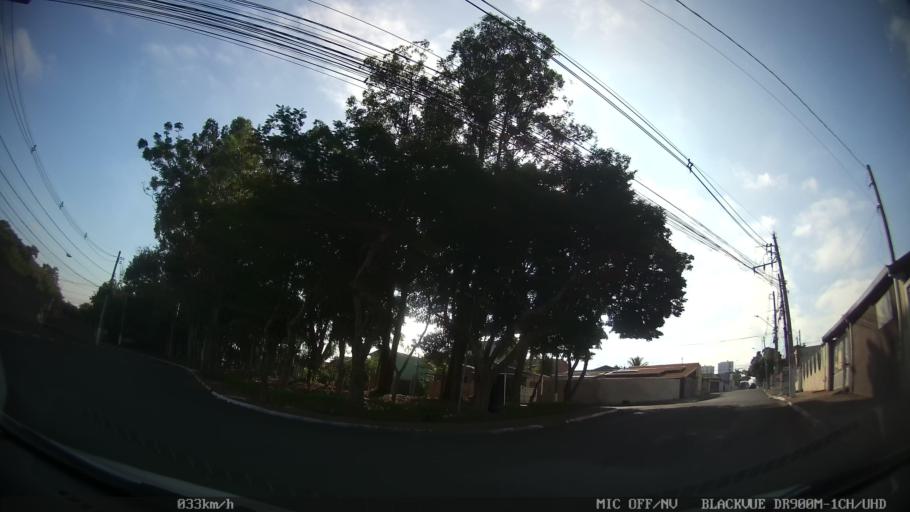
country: BR
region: Sao Paulo
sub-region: Hortolandia
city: Hortolandia
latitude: -22.9075
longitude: -47.1799
